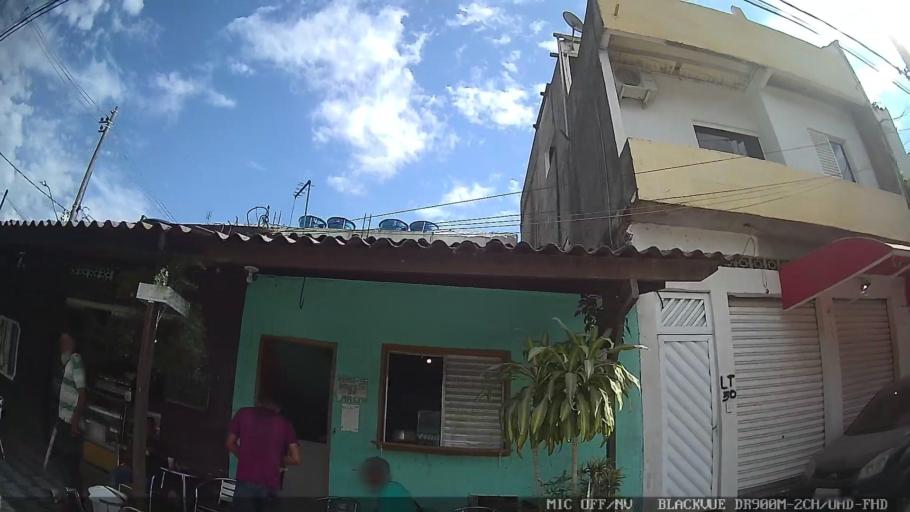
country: BR
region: Sao Paulo
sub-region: Guaruja
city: Guaruja
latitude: -23.9619
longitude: -46.2438
